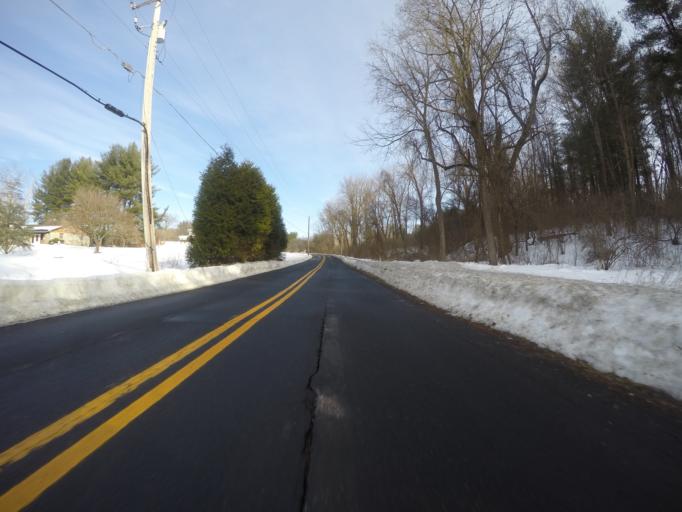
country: US
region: Maryland
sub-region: Baltimore County
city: Hunt Valley
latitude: 39.5710
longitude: -76.6368
